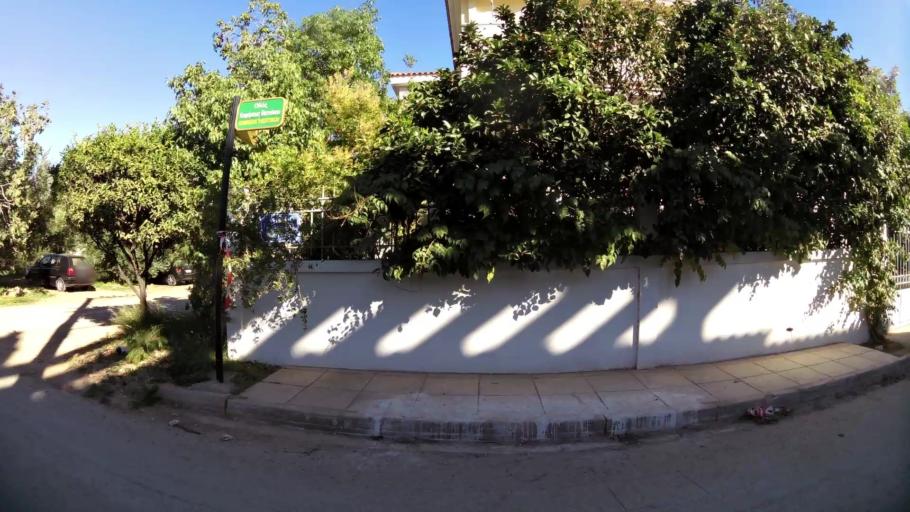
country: GR
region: Attica
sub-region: Nomarchia Anatolikis Attikis
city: Vari
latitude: 37.8360
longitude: 23.8122
